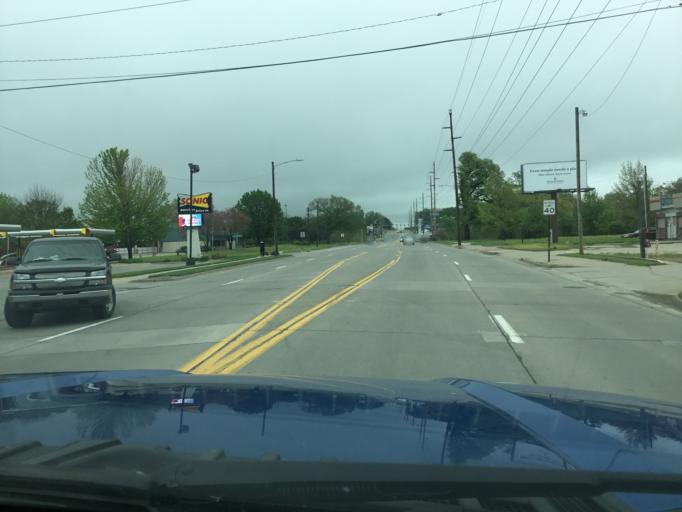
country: US
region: Kansas
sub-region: Shawnee County
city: Topeka
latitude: 39.0297
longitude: -95.6885
